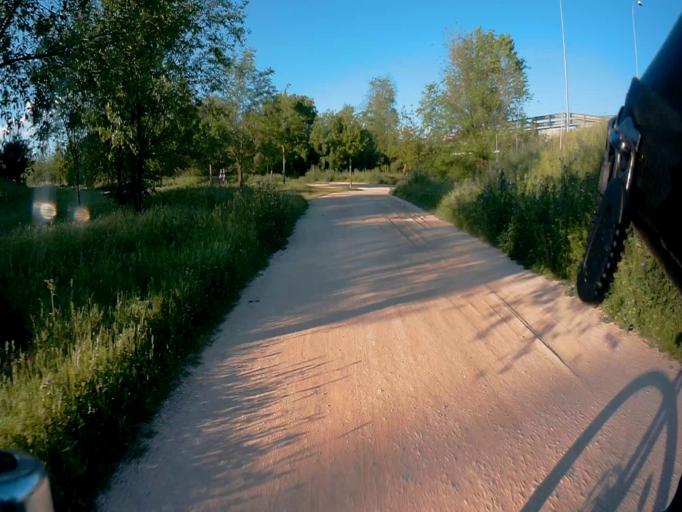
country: ES
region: Madrid
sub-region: Provincia de Madrid
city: Fuenlabrada
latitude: 40.3160
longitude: -3.7949
